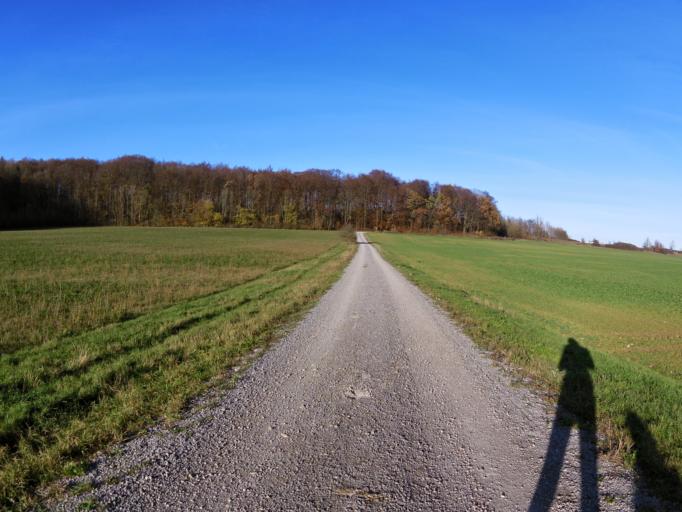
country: DE
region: Thuringia
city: Weberstedt
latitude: 51.0659
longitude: 10.4585
